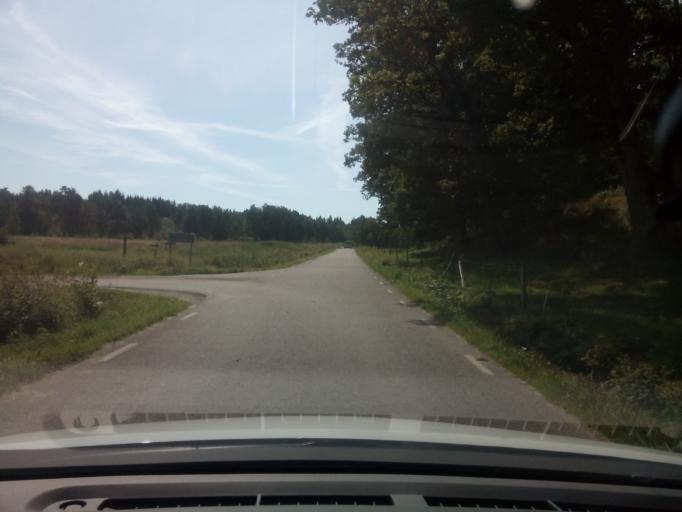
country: SE
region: Soedermanland
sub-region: Trosa Kommun
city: Trosa
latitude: 58.8068
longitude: 17.3638
